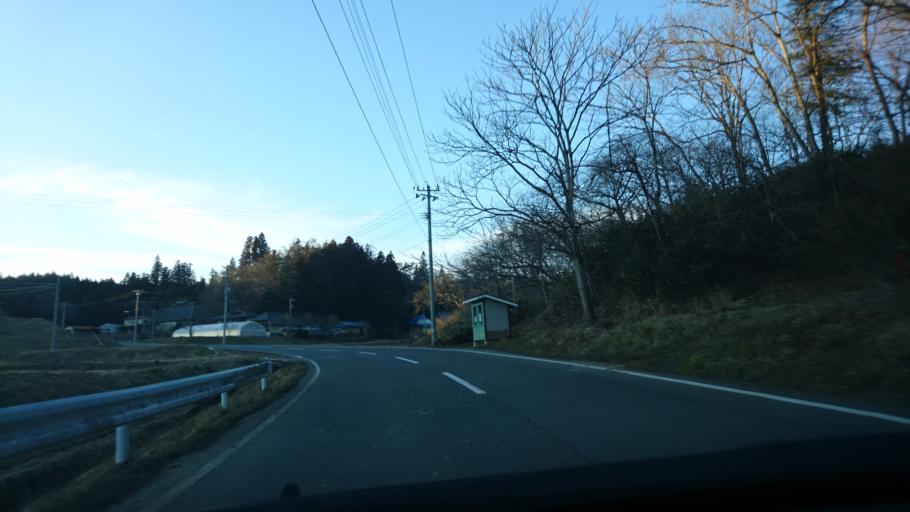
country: JP
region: Iwate
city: Mizusawa
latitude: 39.0435
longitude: 141.3400
